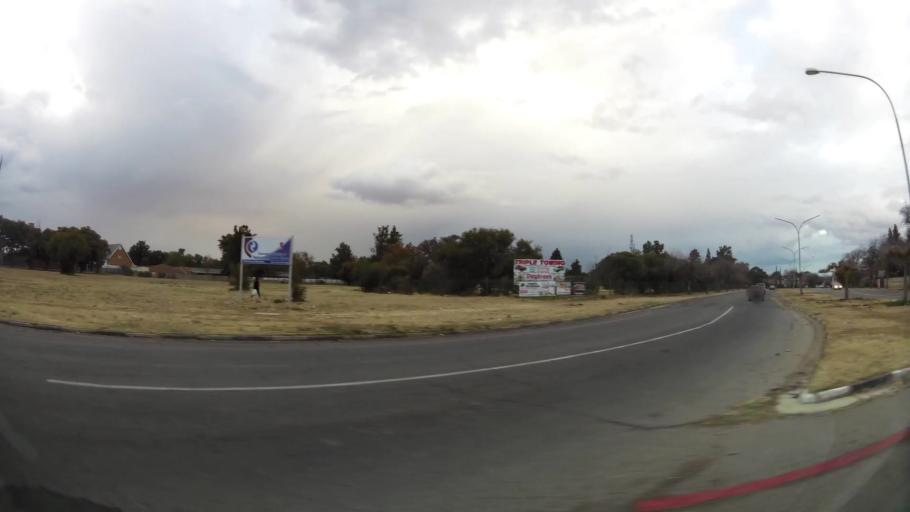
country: ZA
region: Orange Free State
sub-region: Lejweleputswa District Municipality
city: Welkom
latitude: -27.9640
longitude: 26.7397
